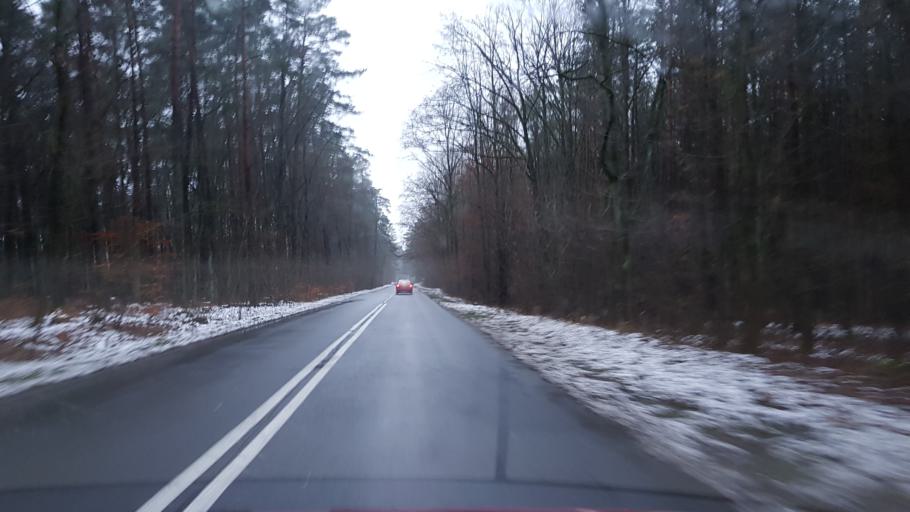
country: PL
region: West Pomeranian Voivodeship
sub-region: Powiat policki
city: Police
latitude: 53.5053
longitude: 14.4924
